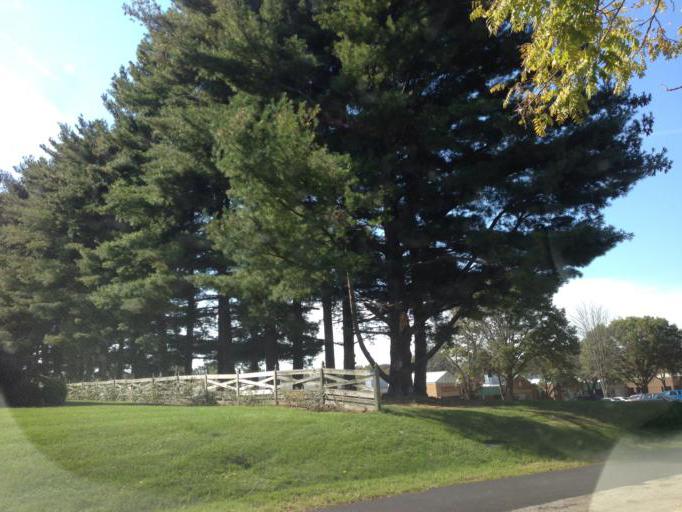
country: US
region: Maryland
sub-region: Howard County
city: Columbia
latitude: 39.2566
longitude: -76.8291
